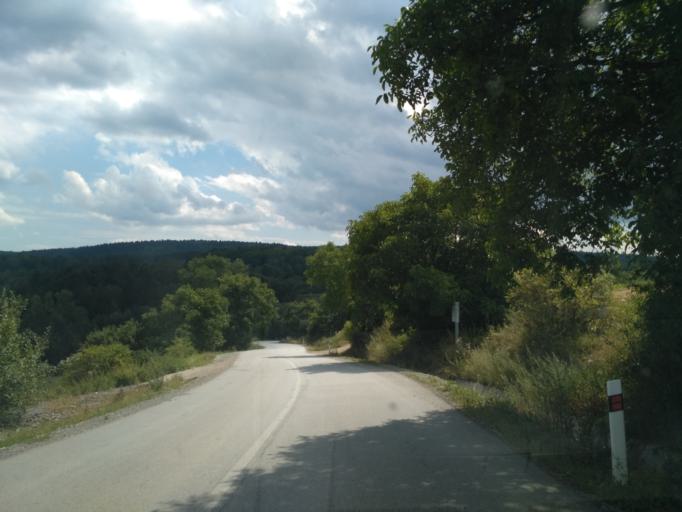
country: SK
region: Kosicky
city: Gelnica
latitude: 48.9267
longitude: 21.0491
